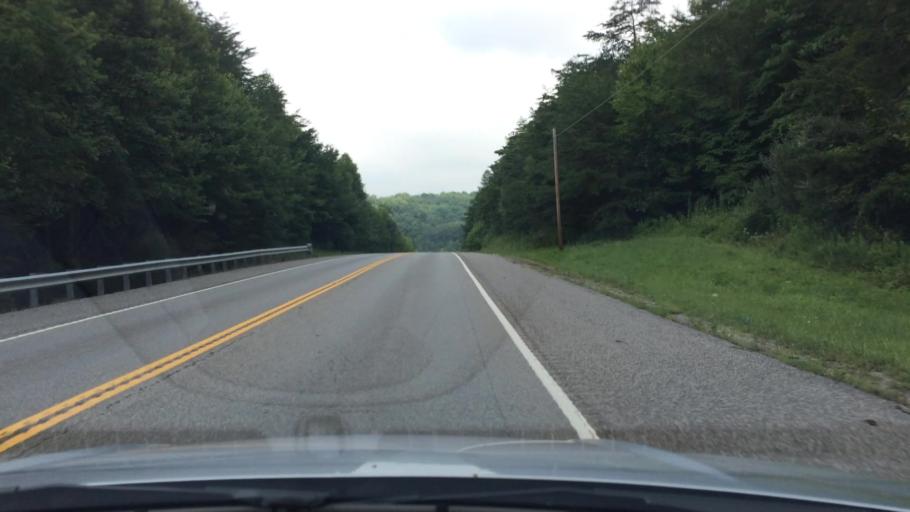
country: US
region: Tennessee
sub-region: Campbell County
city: Caryville
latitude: 36.3964
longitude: -84.2689
